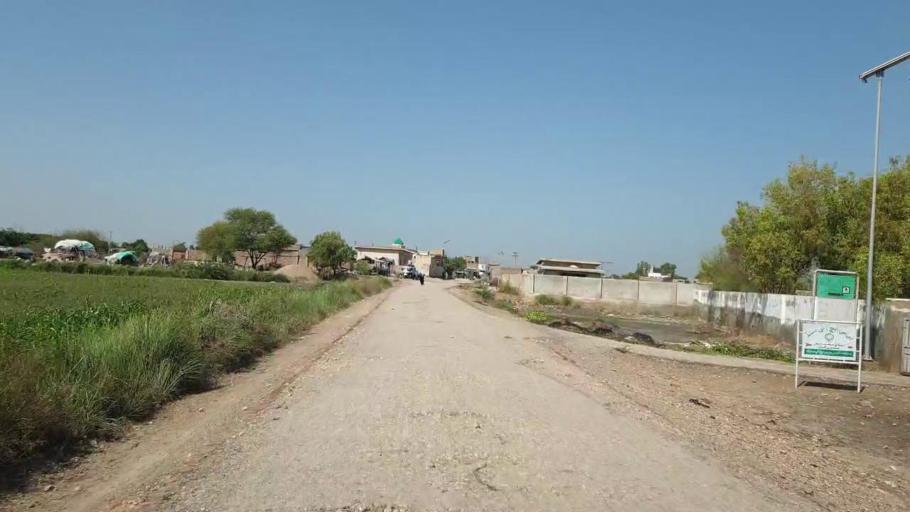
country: PK
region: Sindh
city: Matiari
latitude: 25.4985
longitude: 68.4636
